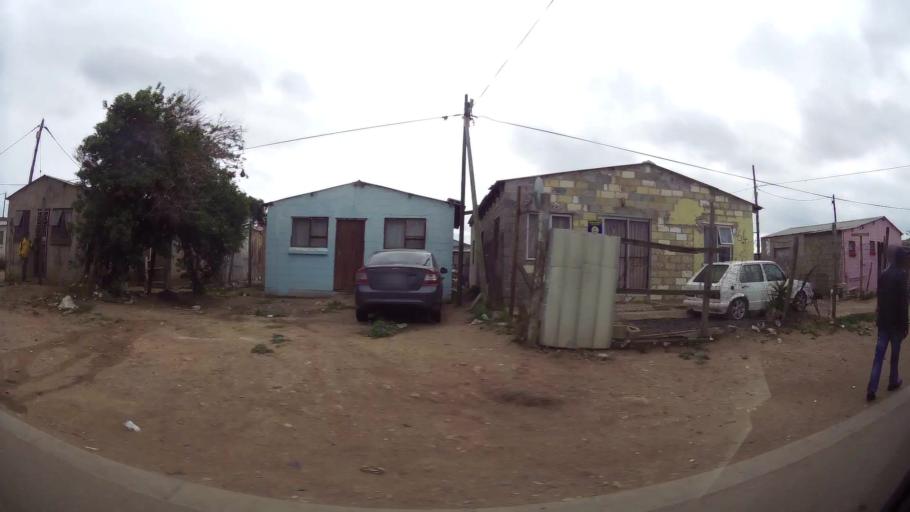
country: ZA
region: Eastern Cape
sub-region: Nelson Mandela Bay Metropolitan Municipality
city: Port Elizabeth
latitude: -33.8865
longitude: 25.5546
